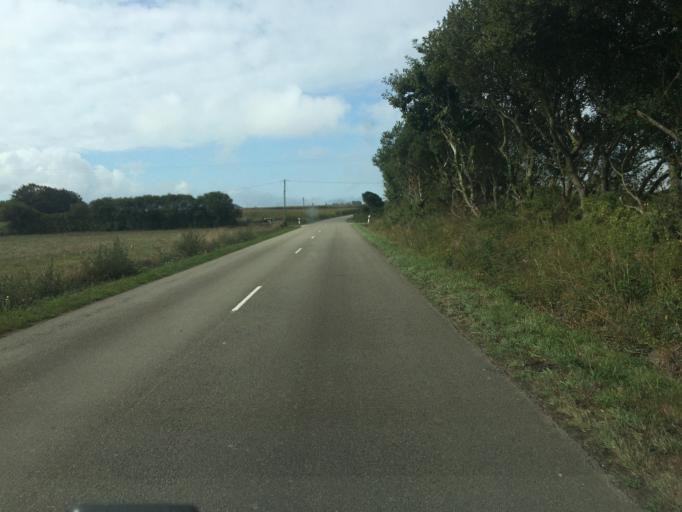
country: FR
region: Brittany
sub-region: Departement du Finistere
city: Beuzec-Cap-Sizun
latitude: 48.0716
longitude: -4.5383
